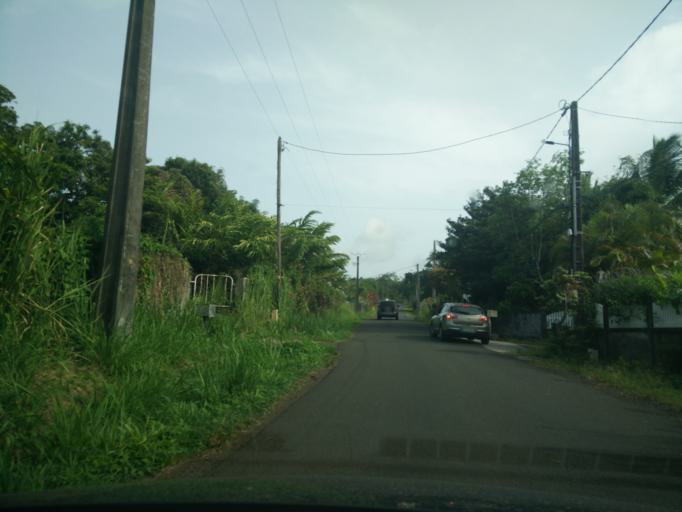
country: GP
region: Guadeloupe
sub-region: Guadeloupe
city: Petit-Bourg
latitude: 16.1247
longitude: -61.5944
